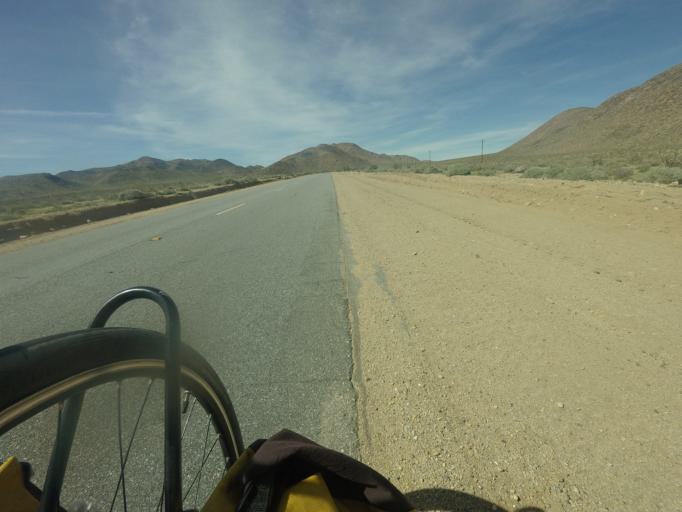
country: US
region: California
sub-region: San Bernardino County
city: Searles Valley
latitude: 35.5779
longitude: -117.4562
